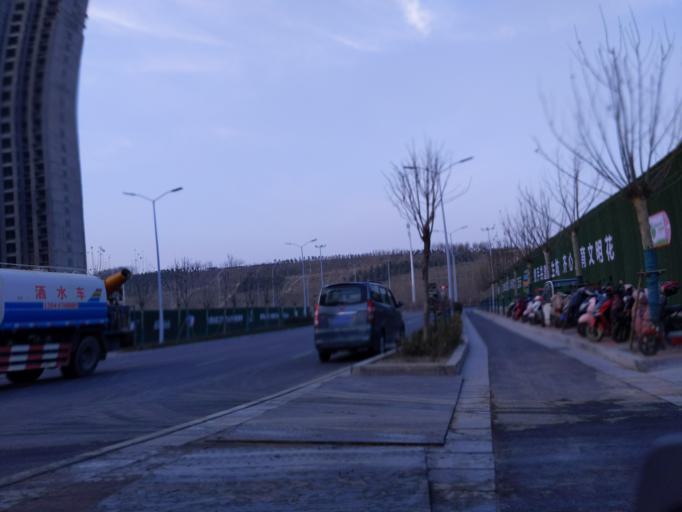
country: CN
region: Henan Sheng
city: Puyang
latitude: 35.8165
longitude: 115.0118
